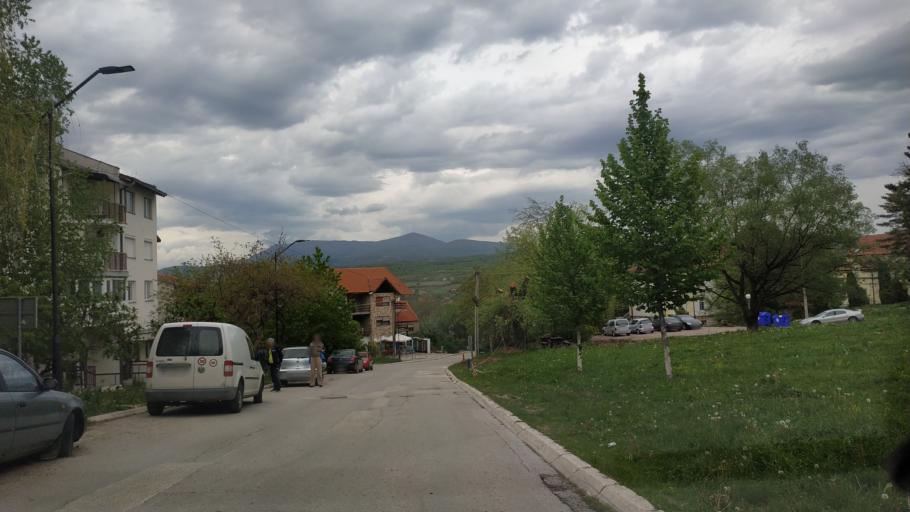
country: RS
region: Central Serbia
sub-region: Zajecarski Okrug
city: Soko Banja
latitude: 43.6404
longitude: 21.8705
